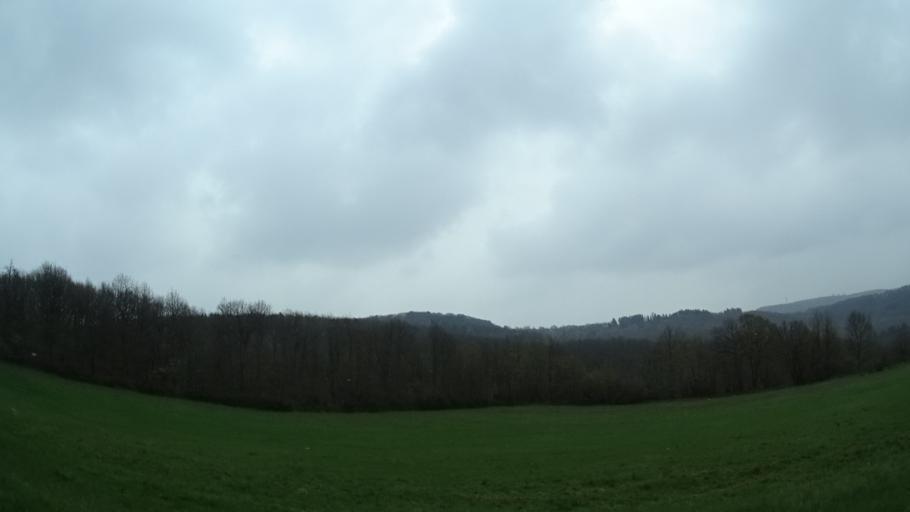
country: DE
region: Rheinland-Pfalz
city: Vollmersbach
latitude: 49.7336
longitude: 7.3170
